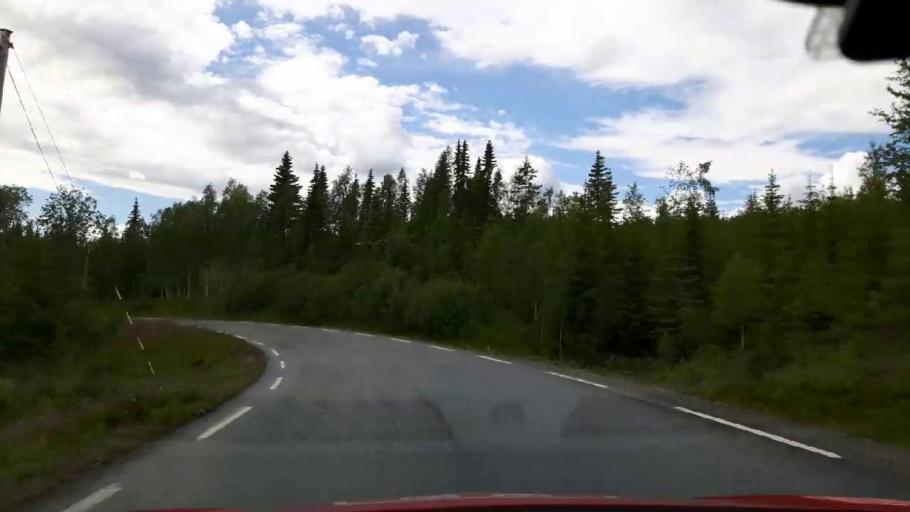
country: NO
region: Nord-Trondelag
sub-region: Lierne
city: Sandvika
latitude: 64.1032
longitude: 14.0196
